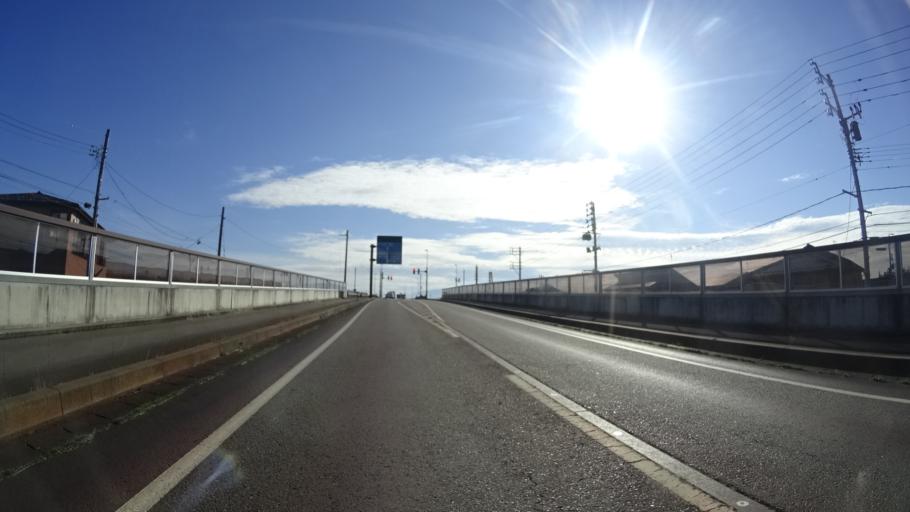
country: JP
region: Niigata
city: Mitsuke
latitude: 37.5461
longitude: 138.8802
